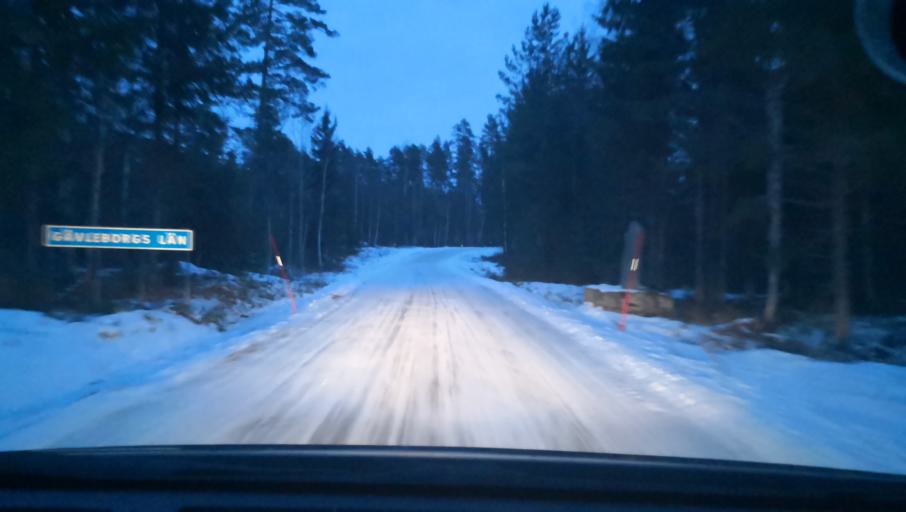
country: SE
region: Dalarna
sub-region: Avesta Kommun
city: Horndal
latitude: 60.2311
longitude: 16.6485
